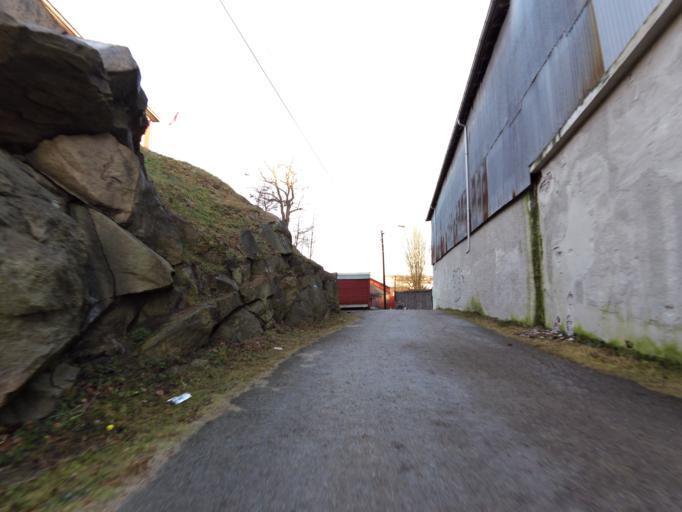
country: NO
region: Ostfold
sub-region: Fredrikstad
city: Fredrikstad
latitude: 59.2191
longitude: 10.9135
